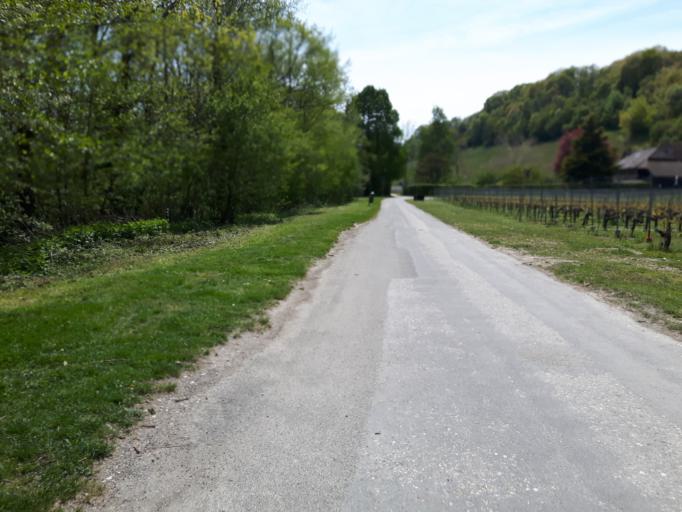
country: CH
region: Neuchatel
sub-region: Boudry District
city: Cortaillod
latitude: 46.9335
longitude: 6.8397
